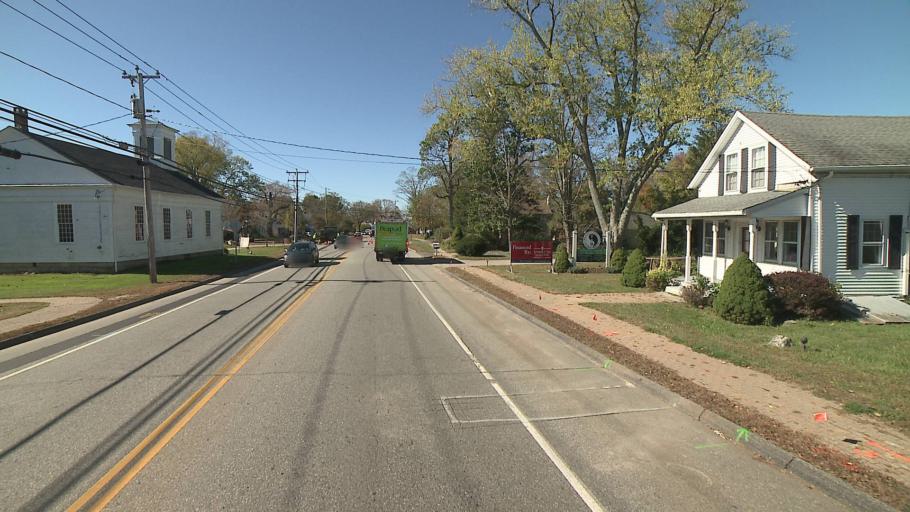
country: US
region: Connecticut
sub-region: Tolland County
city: Hebron
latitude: 41.6588
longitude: -72.3635
